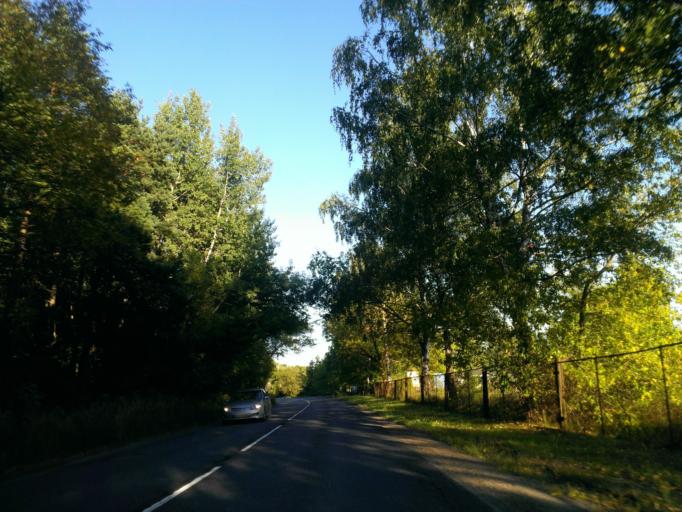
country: LV
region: Riga
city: Bergi
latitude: 57.0039
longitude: 24.2552
